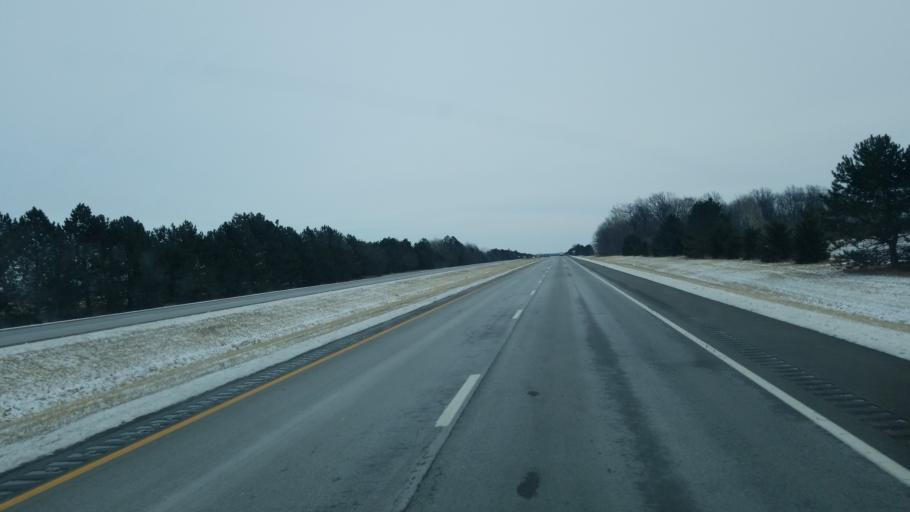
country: US
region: Ohio
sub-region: Wyandot County
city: Carey
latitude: 40.9620
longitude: -83.4654
